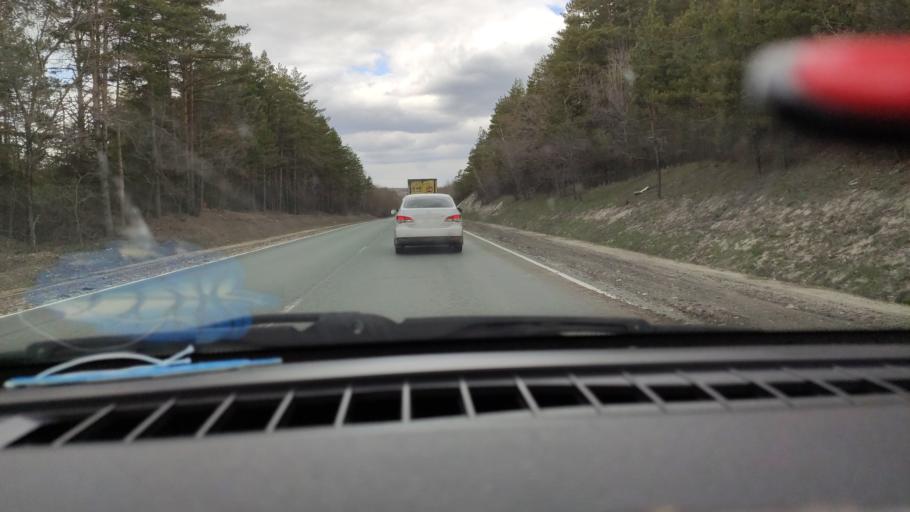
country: RU
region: Saratov
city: Vol'sk
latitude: 52.1056
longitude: 47.4351
